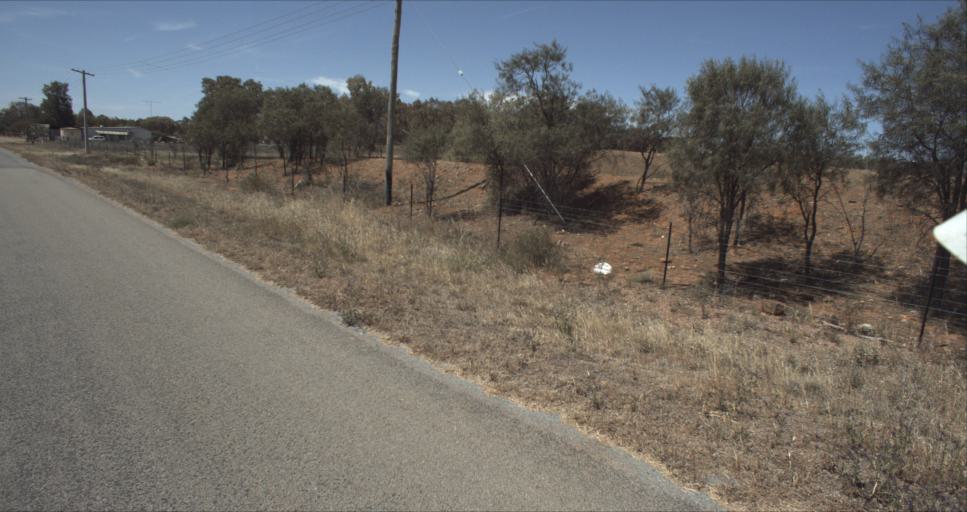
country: AU
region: New South Wales
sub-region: Leeton
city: Leeton
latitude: -34.5799
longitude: 146.4319
